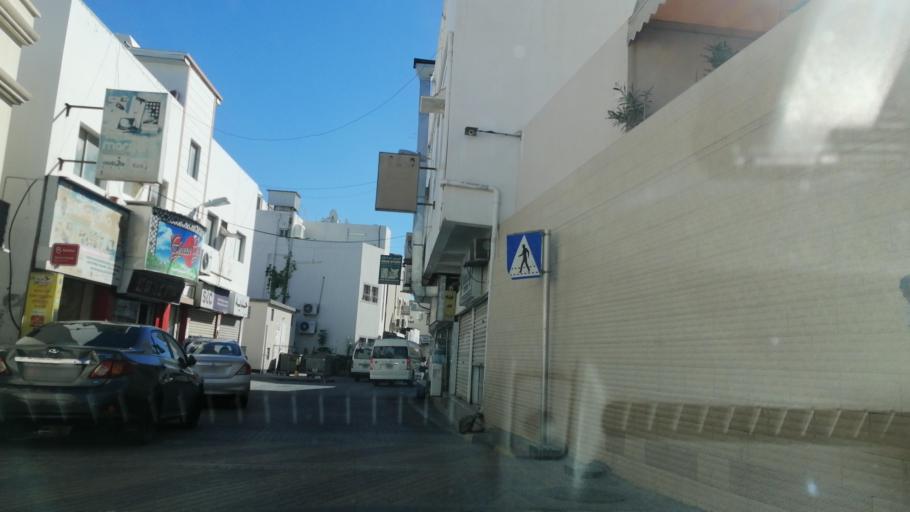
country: BH
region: Muharraq
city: Al Hadd
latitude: 26.2445
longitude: 50.6540
